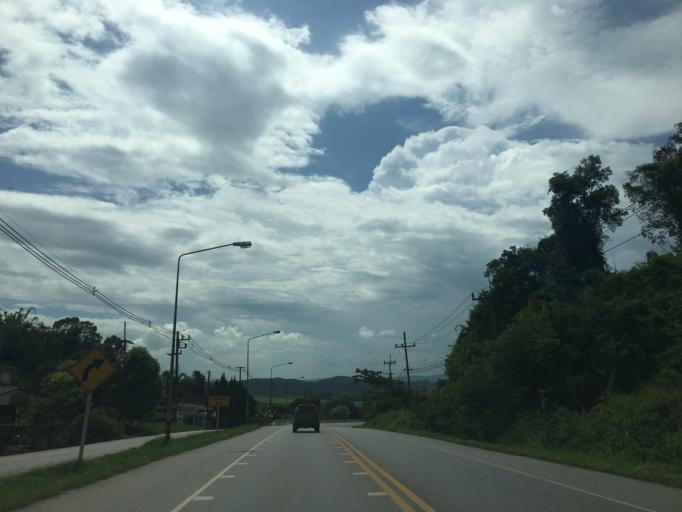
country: TH
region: Chiang Rai
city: Pa Daet
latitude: 19.6552
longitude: 99.9354
